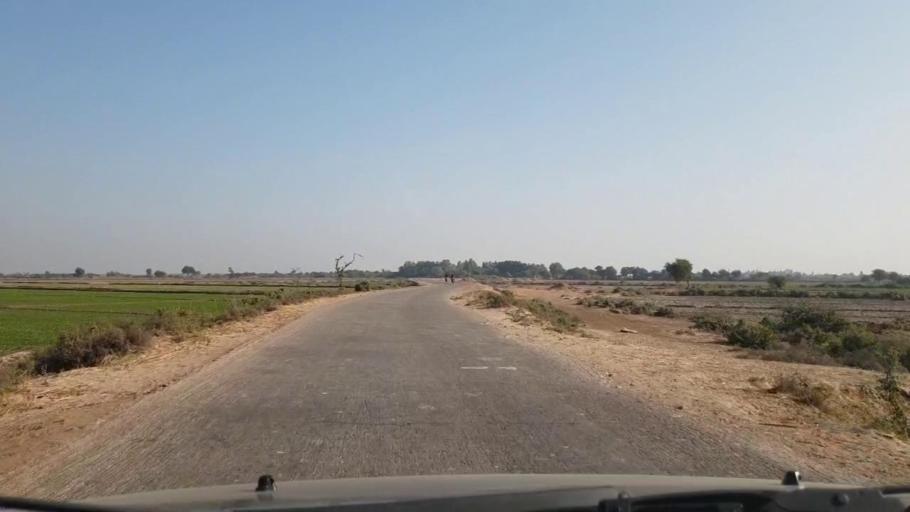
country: PK
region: Sindh
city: Tando Bago
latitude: 24.8706
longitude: 69.0561
